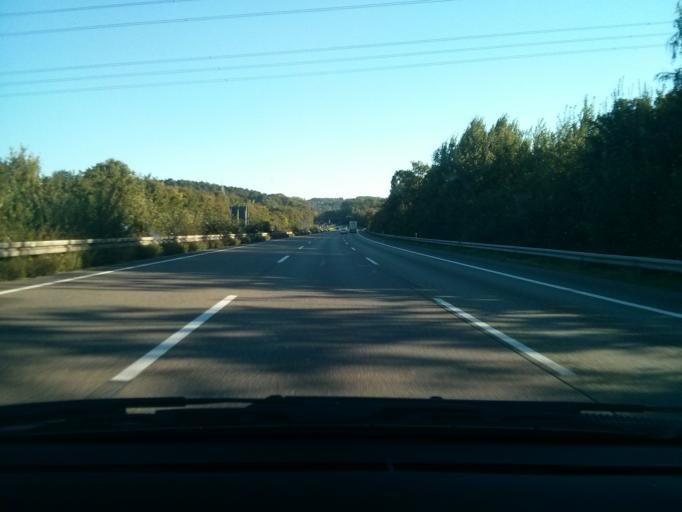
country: DE
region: North Rhine-Westphalia
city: Herdecke
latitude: 51.4561
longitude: 7.4219
